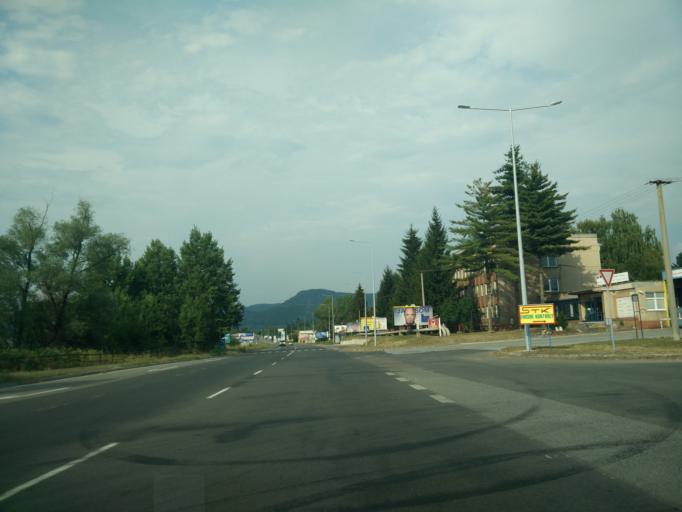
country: SK
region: Banskobystricky
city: Ziar nad Hronom
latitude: 48.5712
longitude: 18.8665
